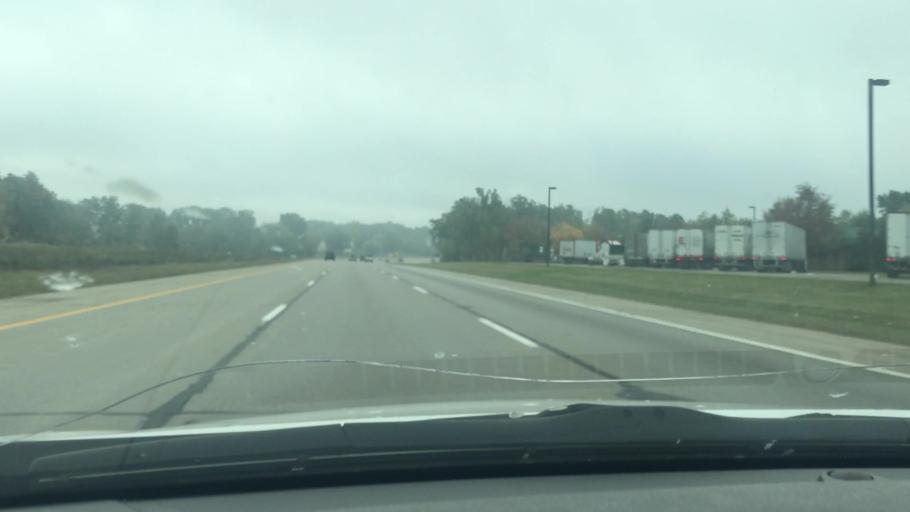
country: US
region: Michigan
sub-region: Livingston County
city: Howell
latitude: 42.6053
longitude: -83.9590
